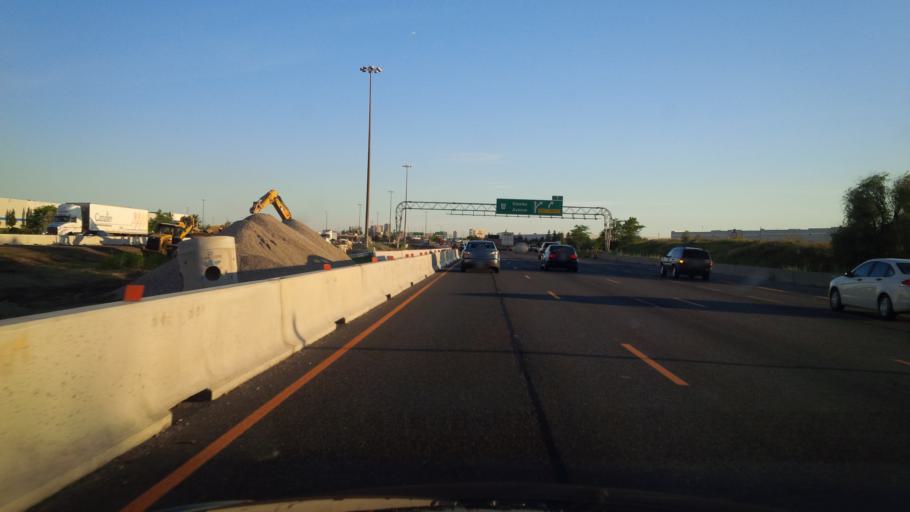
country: CA
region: Ontario
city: Brampton
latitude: 43.6790
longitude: -79.7062
